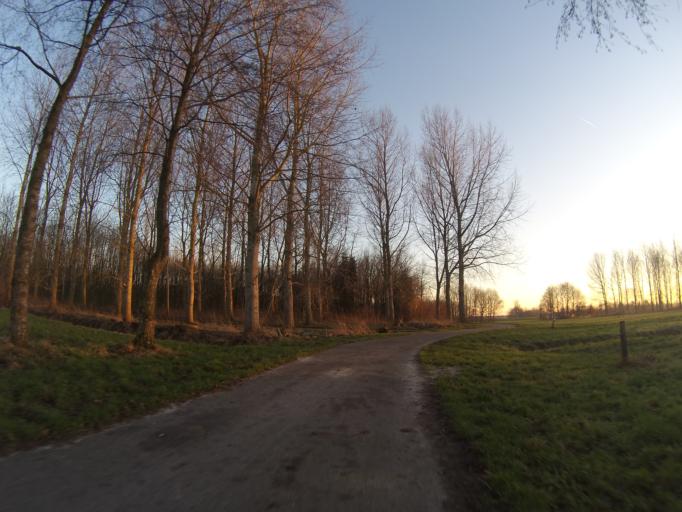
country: NL
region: Drenthe
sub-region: Gemeente Emmen
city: Emmen
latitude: 52.7423
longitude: 6.9043
